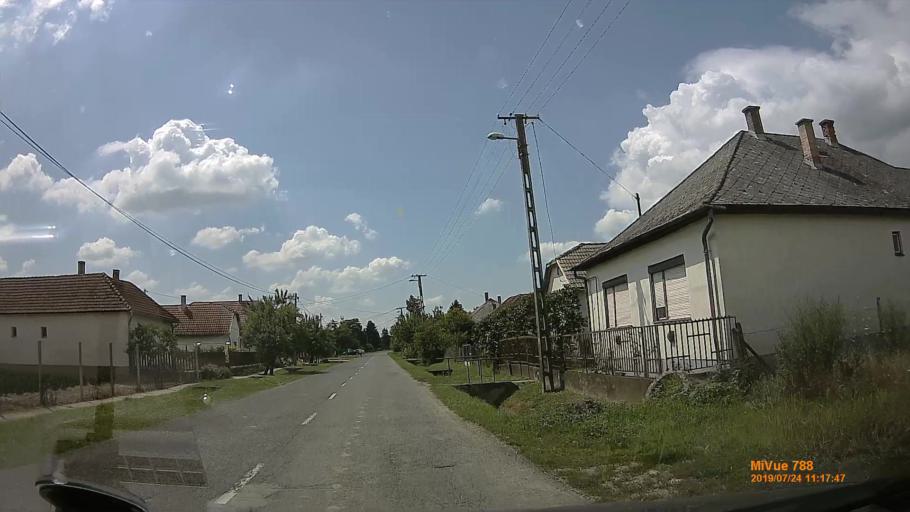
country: HU
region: Szabolcs-Szatmar-Bereg
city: Tarpa
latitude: 48.1671
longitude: 22.4593
